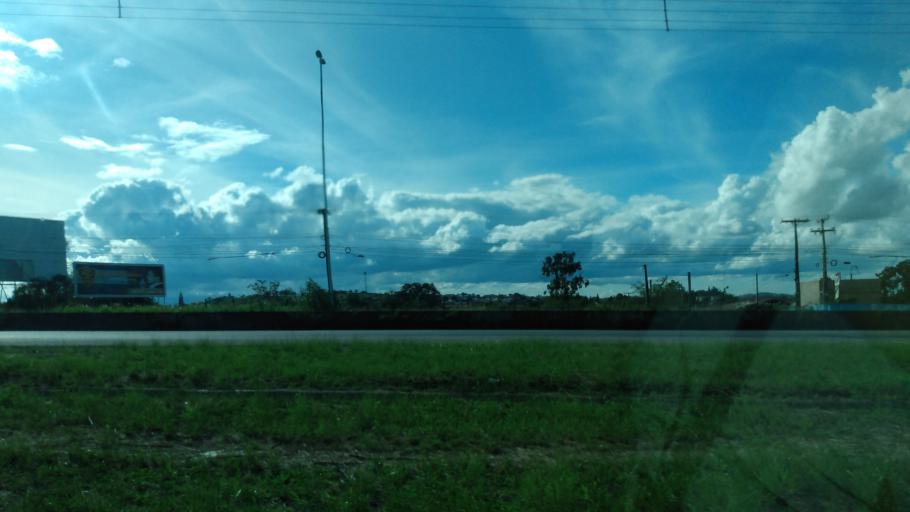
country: ET
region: Oromiya
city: Gore
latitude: 8.1993
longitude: 35.5869
